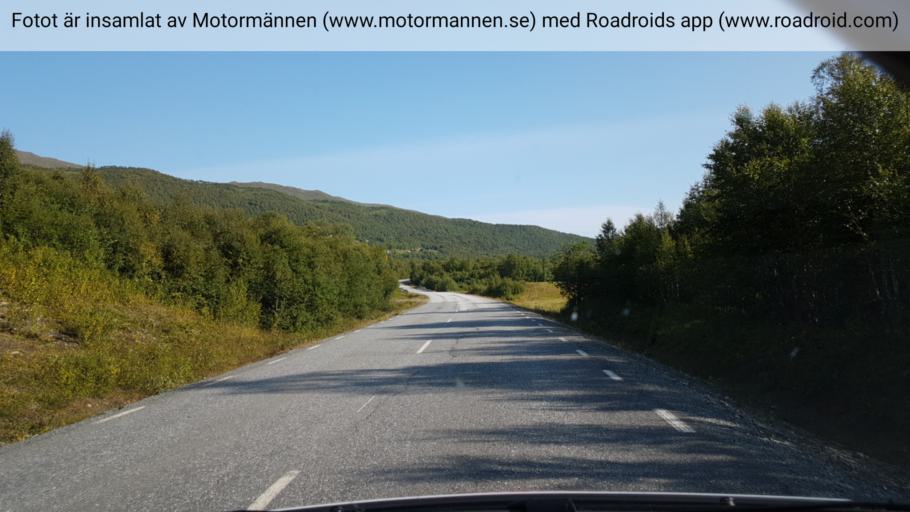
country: NO
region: Nordland
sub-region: Rana
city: Mo i Rana
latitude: 65.7820
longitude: 15.1193
